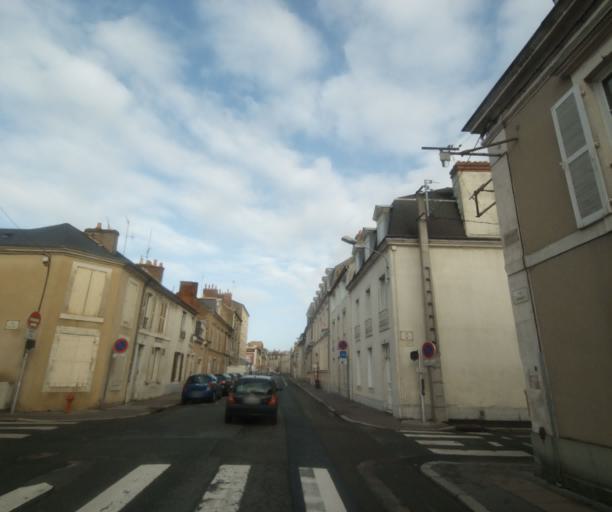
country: FR
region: Pays de la Loire
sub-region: Departement de la Sarthe
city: Le Mans
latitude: 47.9981
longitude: 0.2031
